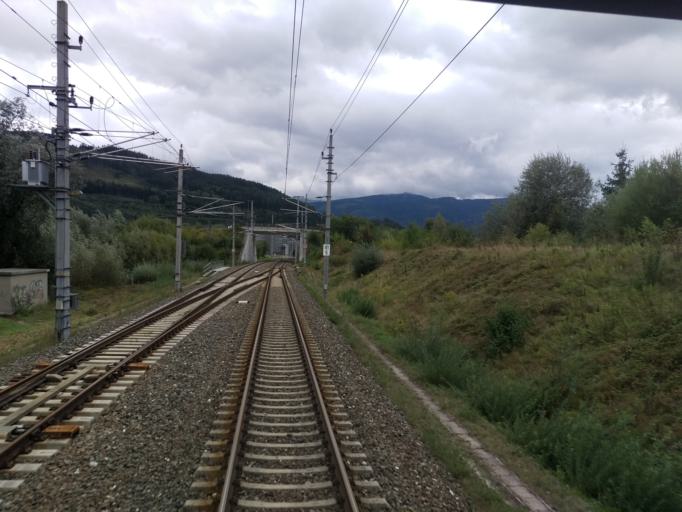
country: AT
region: Styria
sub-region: Politischer Bezirk Liezen
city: Stainach
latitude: 47.5358
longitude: 14.1182
